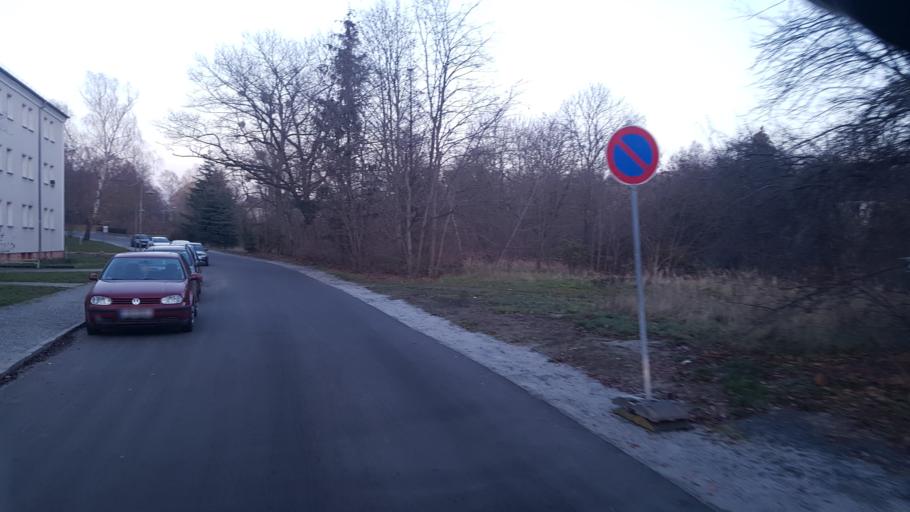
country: DE
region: Brandenburg
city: Lauchhammer
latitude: 51.4985
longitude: 13.7498
